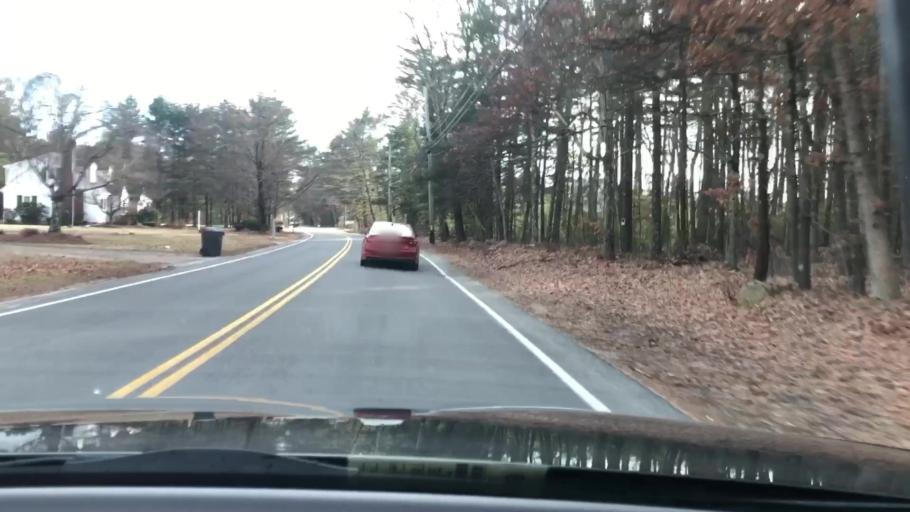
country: US
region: Massachusetts
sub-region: Worcester County
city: Milford
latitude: 42.1077
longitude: -71.5146
